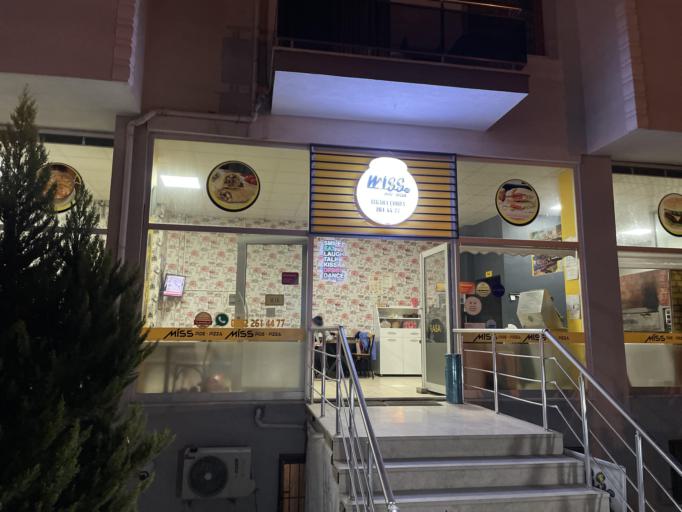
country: TR
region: Denizli
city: Denizli
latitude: 37.7453
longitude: 29.1103
